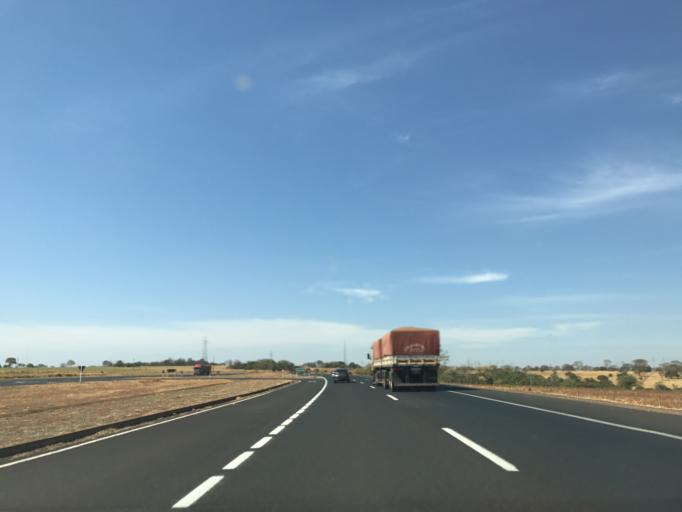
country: BR
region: Minas Gerais
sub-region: Centralina
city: Centralina
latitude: -18.7590
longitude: -49.0766
